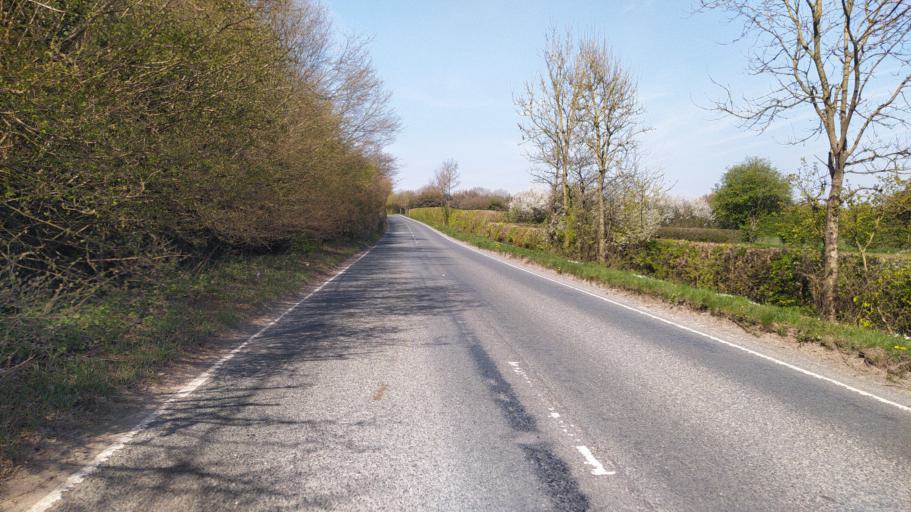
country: GB
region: England
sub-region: Somerset
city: Frome
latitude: 51.2125
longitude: -2.3924
